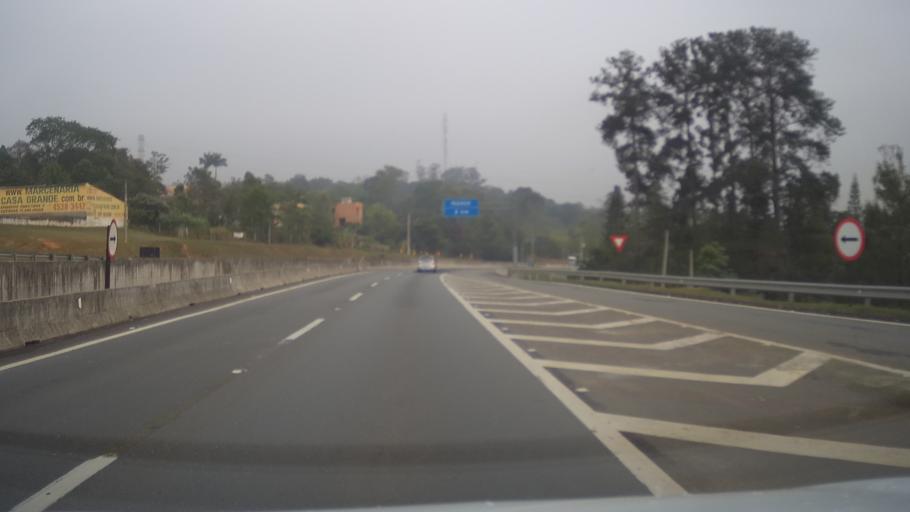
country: BR
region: Sao Paulo
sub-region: Itatiba
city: Itatiba
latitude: -23.0957
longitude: -46.8474
